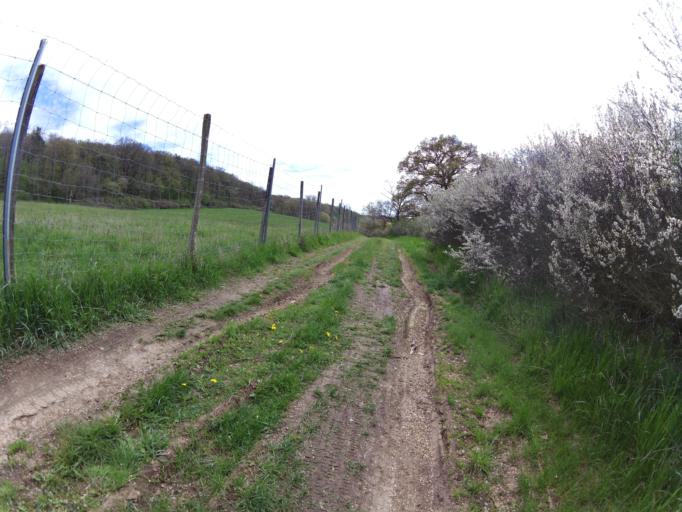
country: DE
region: Bavaria
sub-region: Regierungsbezirk Unterfranken
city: Prosselsheim
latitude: 49.8598
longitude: 10.1451
